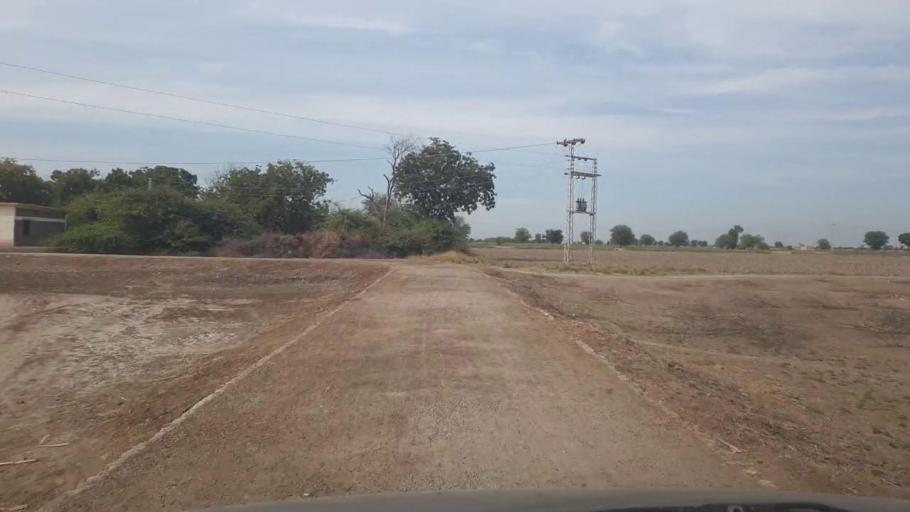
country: PK
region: Sindh
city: Kunri
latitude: 25.2750
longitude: 69.6057
